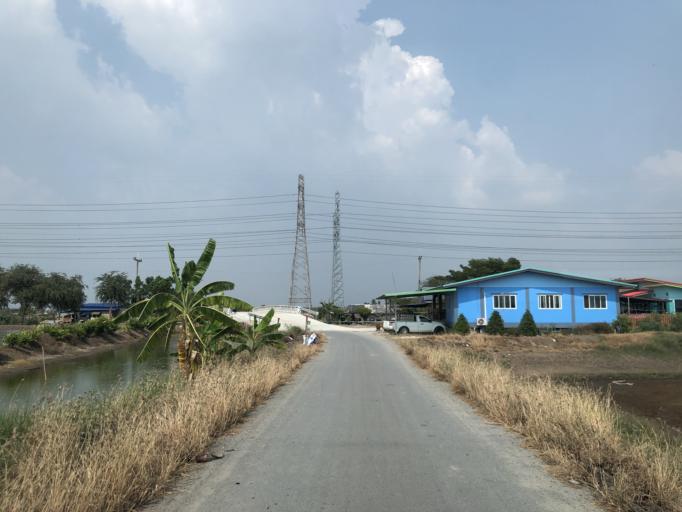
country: TH
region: Samut Prakan
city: Bang Bo
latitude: 13.5438
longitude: 100.8807
